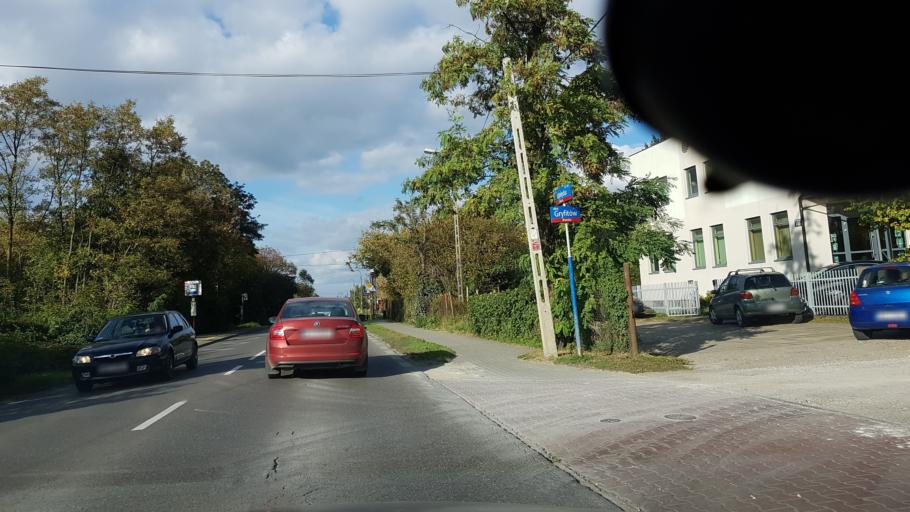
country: PL
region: Masovian Voivodeship
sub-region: Warszawa
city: Targowek
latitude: 52.3030
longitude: 21.0299
